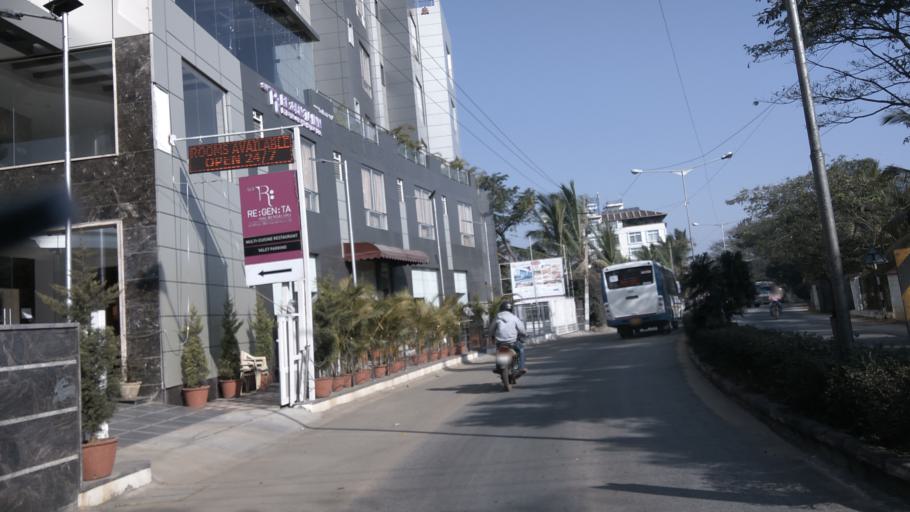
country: IN
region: Karnataka
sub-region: Bangalore Rural
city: Devanhalli
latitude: 13.1915
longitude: 77.6458
